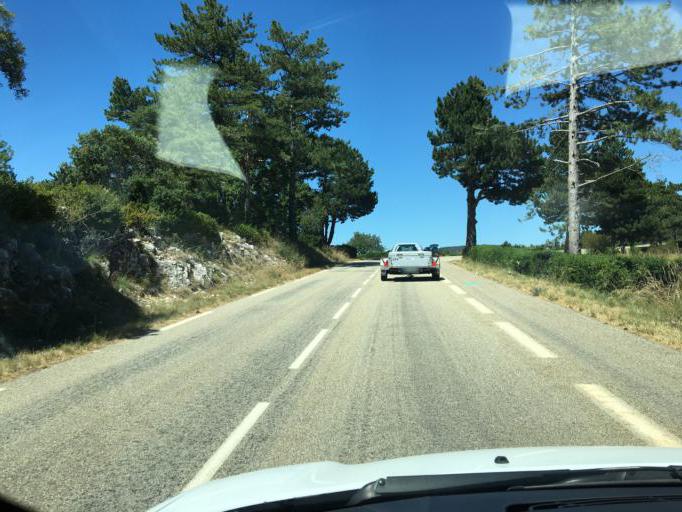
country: FR
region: Provence-Alpes-Cote d'Azur
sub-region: Departement du Vaucluse
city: Bedoin
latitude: 44.1701
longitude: 5.2013
